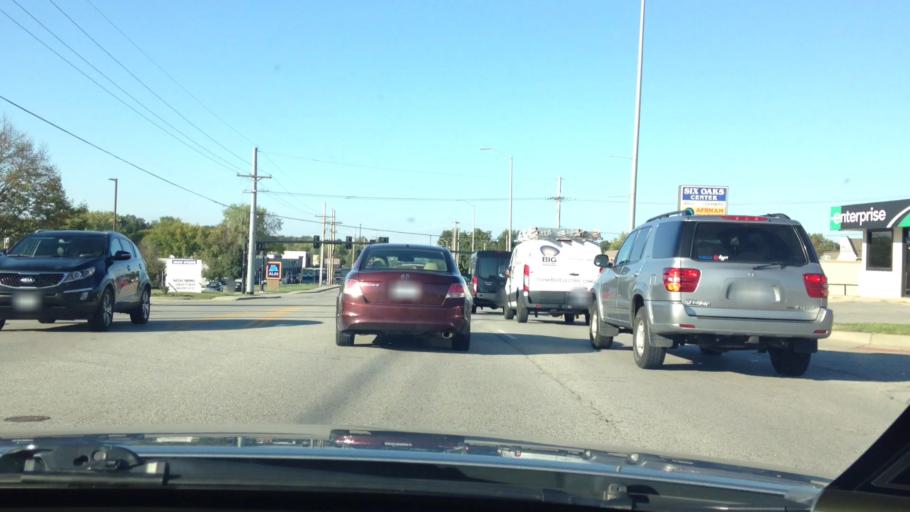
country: US
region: Missouri
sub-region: Clay County
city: Gladstone
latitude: 39.2308
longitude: -94.5761
